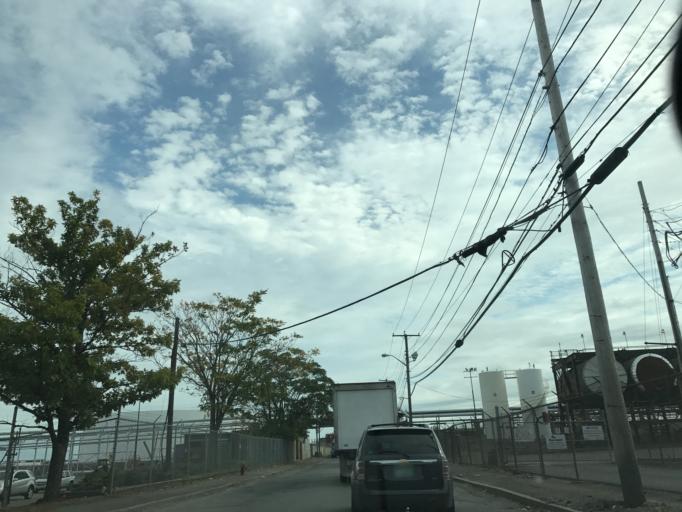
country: US
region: Massachusetts
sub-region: Middlesex County
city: Everett
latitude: 42.3965
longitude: -71.0608
